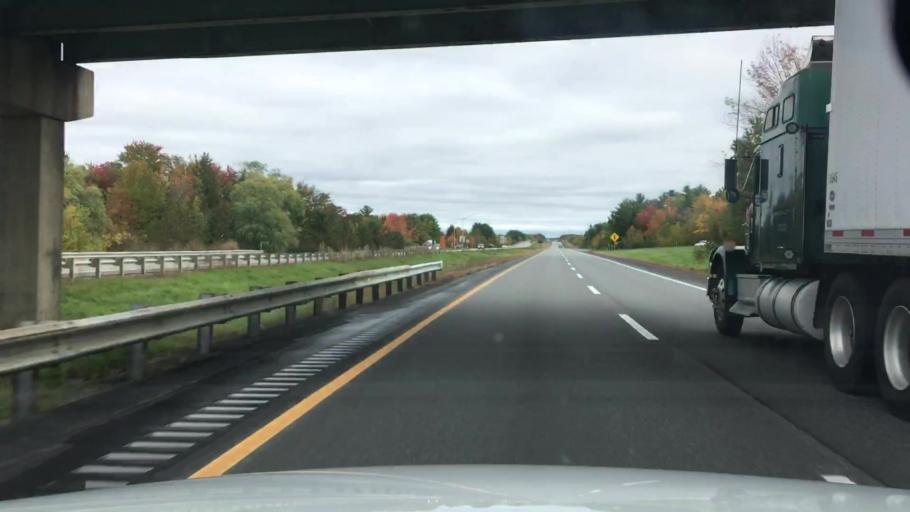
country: US
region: Maine
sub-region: Penobscot County
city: Newport
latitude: 44.8339
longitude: -69.2920
